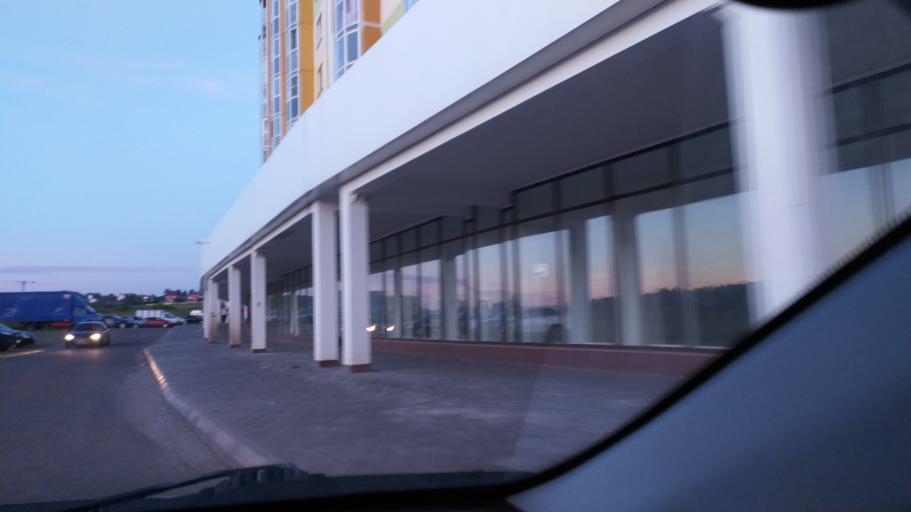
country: RU
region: Chuvashia
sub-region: Cheboksarskiy Rayon
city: Cheboksary
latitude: 56.1207
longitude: 47.2110
